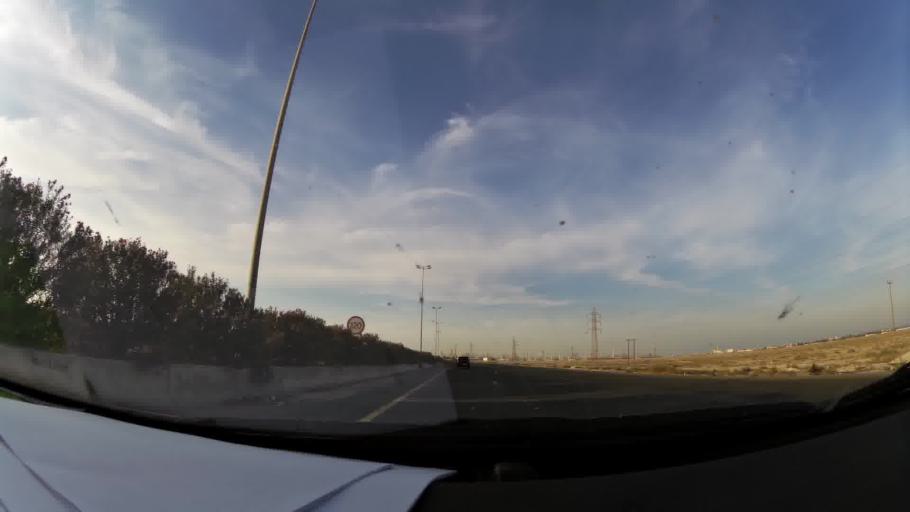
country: KW
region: Al Ahmadi
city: Al Fahahil
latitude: 28.9712
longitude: 48.1620
